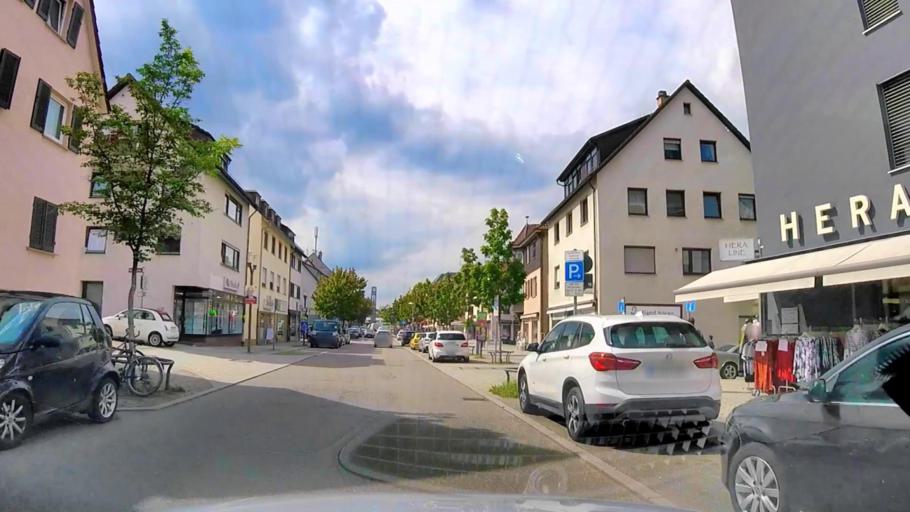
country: DE
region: Baden-Wuerttemberg
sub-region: Regierungsbezirk Stuttgart
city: Korntal
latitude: 48.8140
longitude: 9.1163
